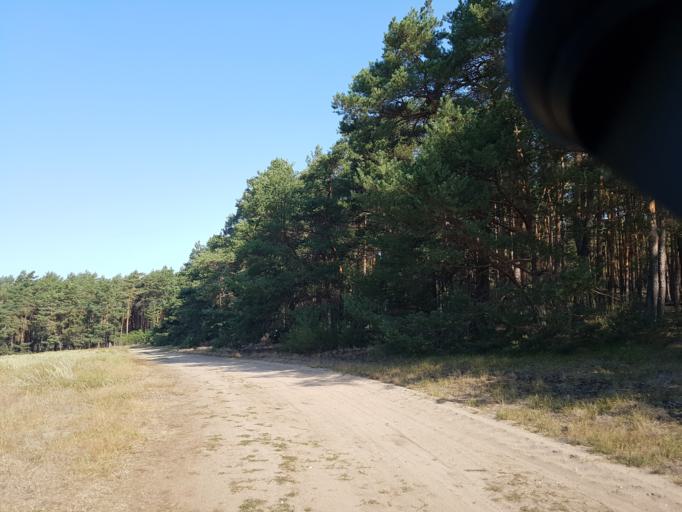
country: DE
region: Brandenburg
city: Wollin
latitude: 52.2522
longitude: 12.4990
